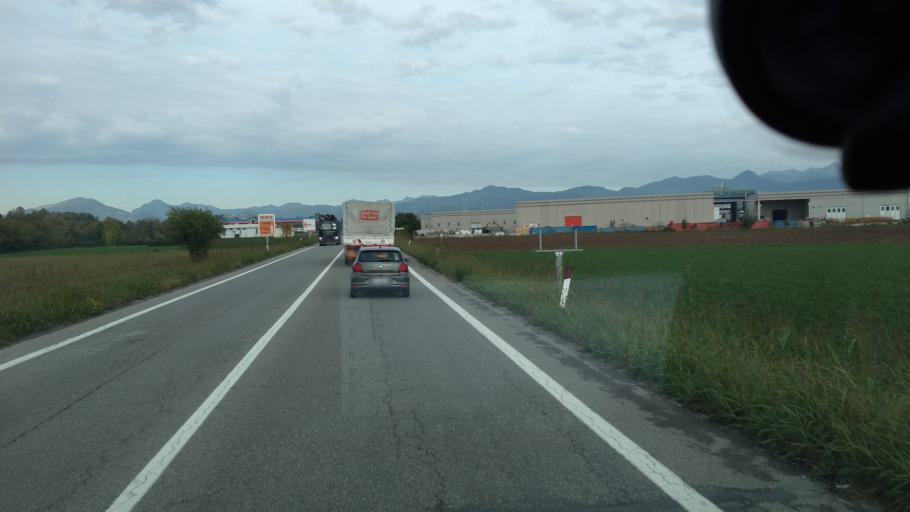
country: IT
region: Lombardy
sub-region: Provincia di Bergamo
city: Grassobbio
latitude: 45.6434
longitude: 9.7091
